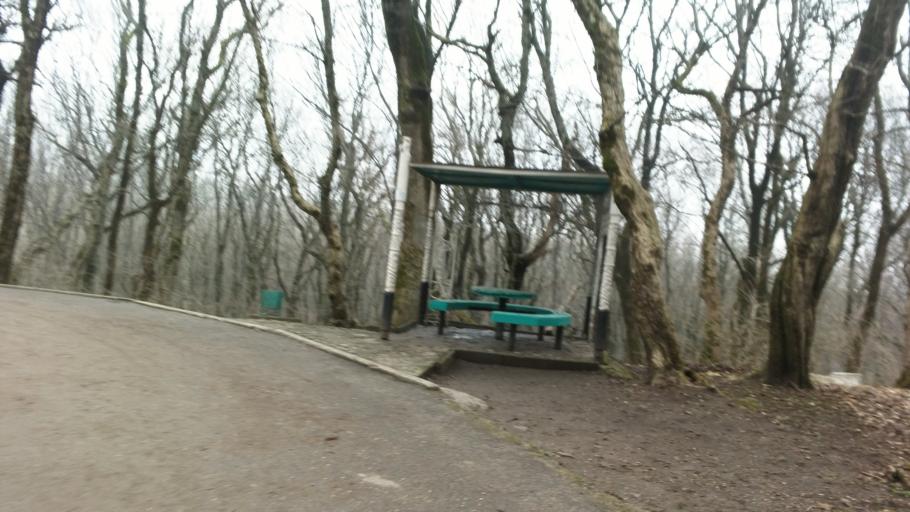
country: RU
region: Stavropol'skiy
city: Zheleznovodsk
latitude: 44.1428
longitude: 43.0348
